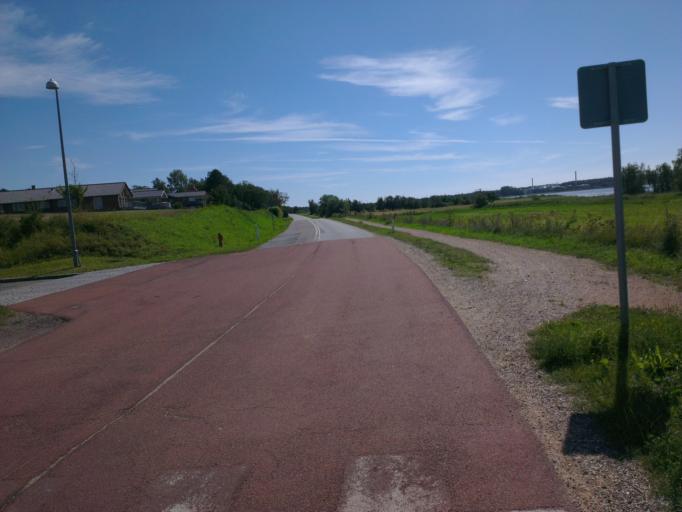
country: DK
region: Capital Region
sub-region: Frederikssund Kommune
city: Frederikssund
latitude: 55.8684
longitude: 12.0678
